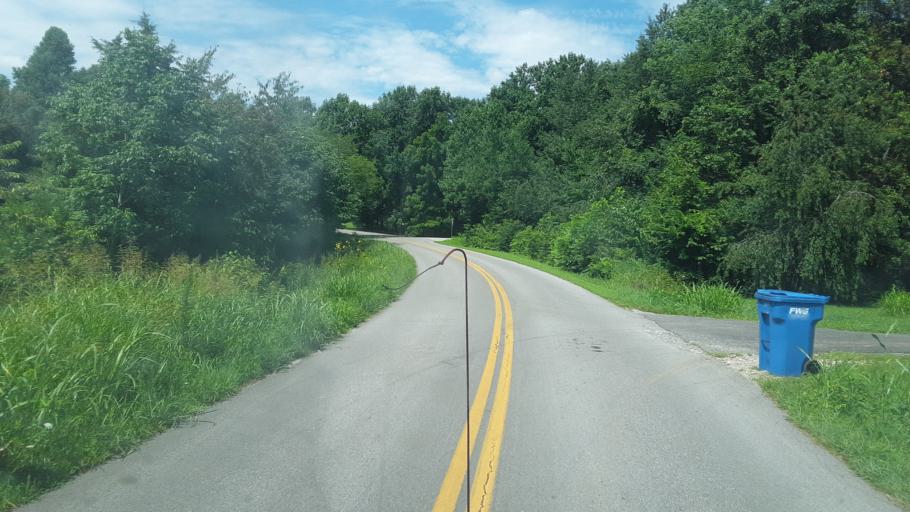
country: US
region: Kentucky
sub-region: Christian County
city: Oak Grove
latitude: 36.7317
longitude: -87.3346
